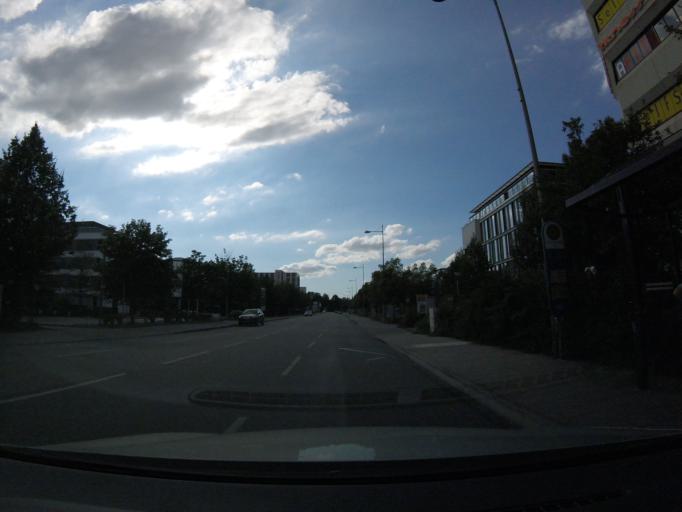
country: DE
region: Bavaria
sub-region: Upper Bavaria
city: Unterfoehring
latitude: 48.1785
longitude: 11.6358
